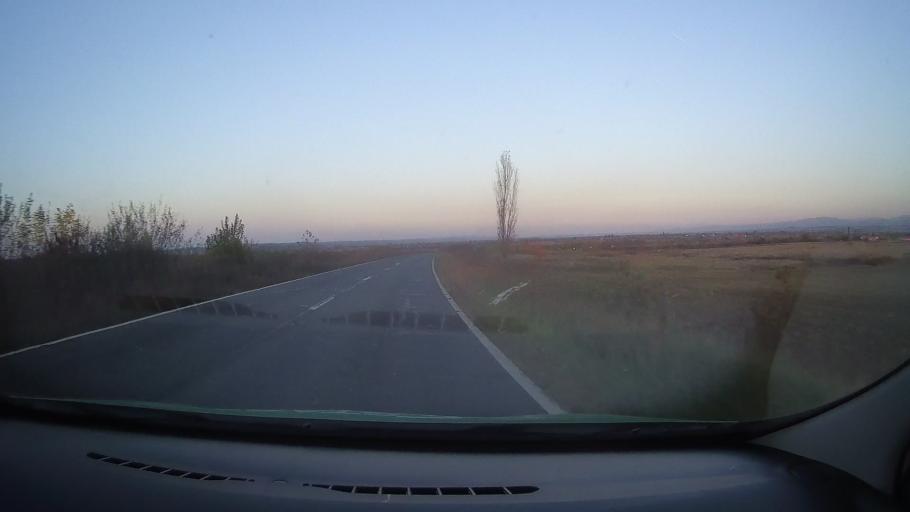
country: RO
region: Timis
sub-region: Comuna Manastiur
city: Manastiur
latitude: 45.8236
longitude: 22.0873
